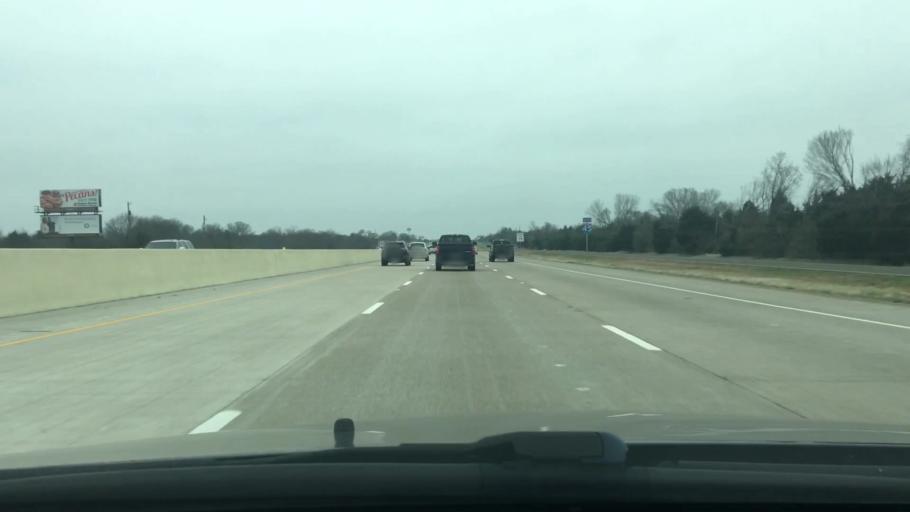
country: US
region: Texas
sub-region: Navarro County
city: Corsicana
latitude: 32.0019
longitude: -96.4313
